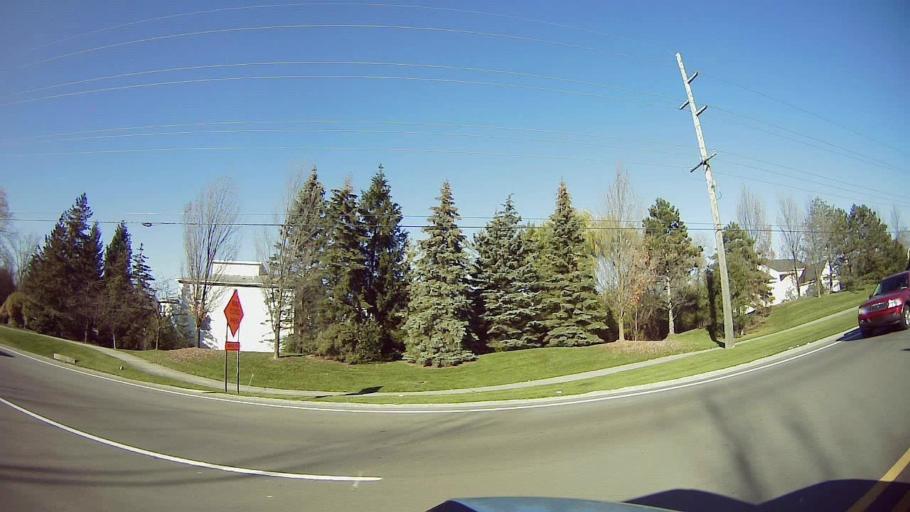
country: US
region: Michigan
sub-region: Oakland County
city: West Bloomfield Township
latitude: 42.5420
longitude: -83.3918
